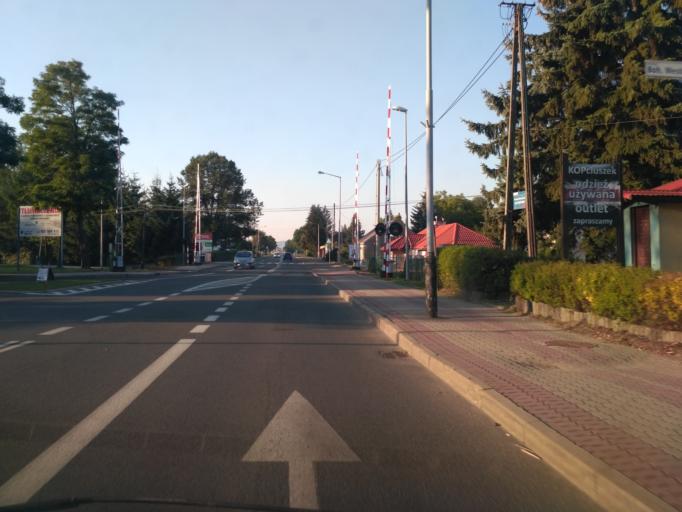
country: PL
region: Subcarpathian Voivodeship
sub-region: Krosno
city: Krosno
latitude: 49.6835
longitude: 21.7717
